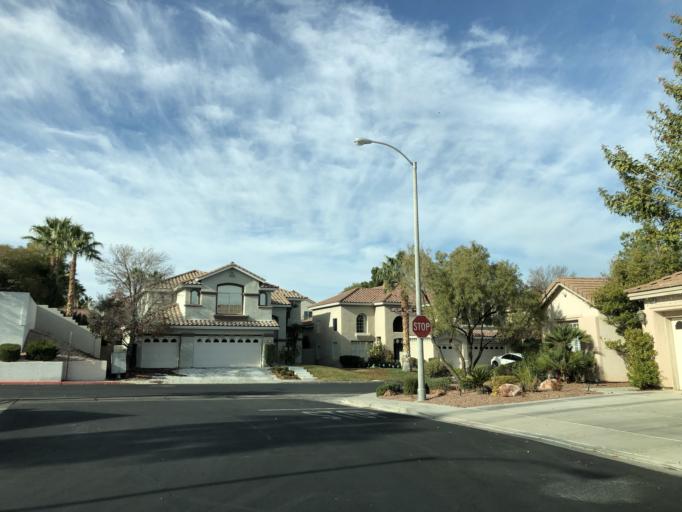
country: US
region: Nevada
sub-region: Clark County
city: Whitney
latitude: 36.0191
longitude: -115.0713
